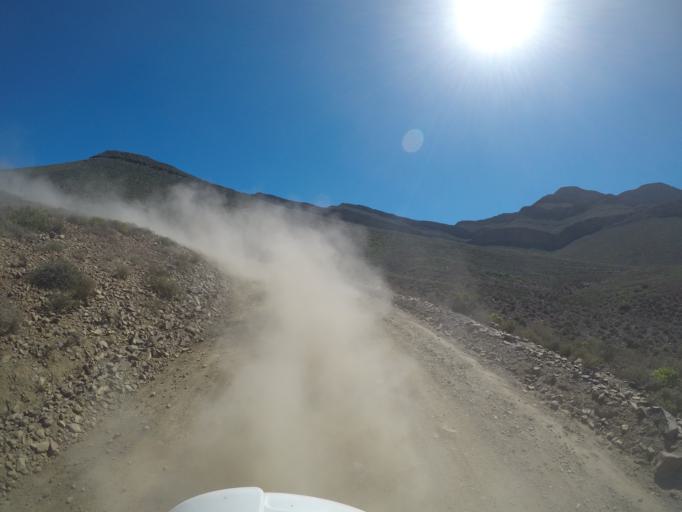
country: ZA
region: Western Cape
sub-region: West Coast District Municipality
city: Clanwilliam
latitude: -32.6191
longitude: 19.3842
